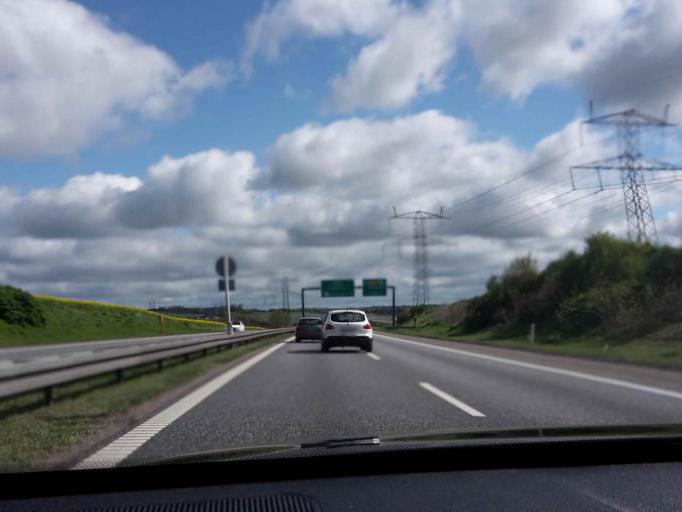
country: DK
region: Central Jutland
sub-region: Favrskov Kommune
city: Soften
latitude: 56.2116
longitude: 10.0917
